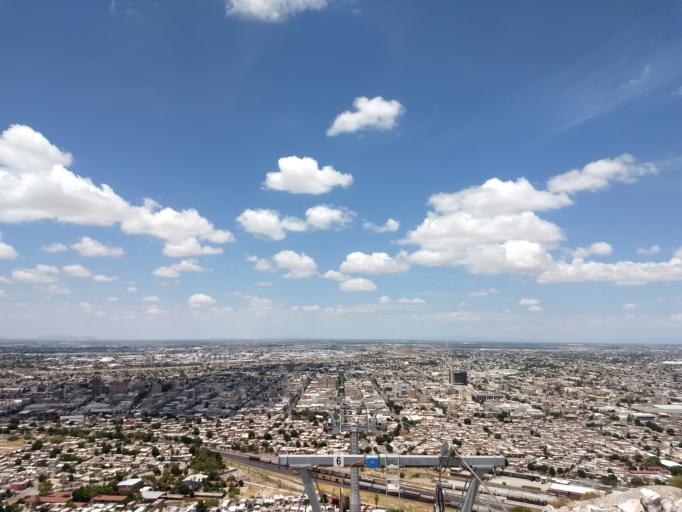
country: MX
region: Durango
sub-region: Lerdo
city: El Huarache (El Guarache)
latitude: 25.5264
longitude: -103.4570
